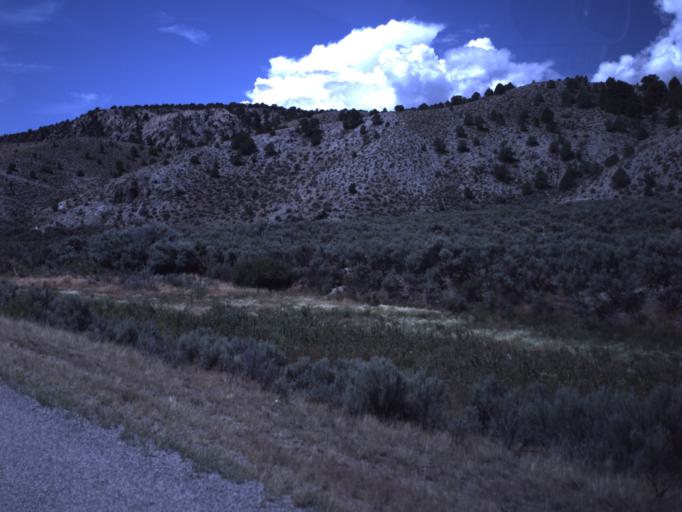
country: US
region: Utah
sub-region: Piute County
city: Junction
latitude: 38.0495
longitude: -112.3535
